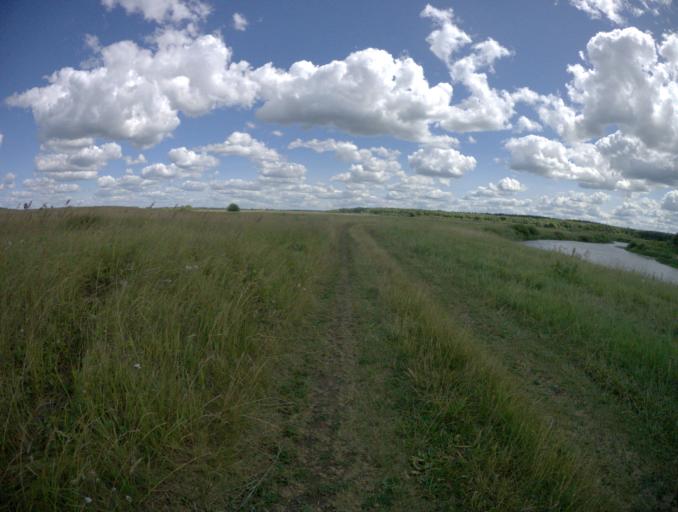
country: RU
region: Vladimir
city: Orgtrud
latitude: 56.3017
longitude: 40.6233
